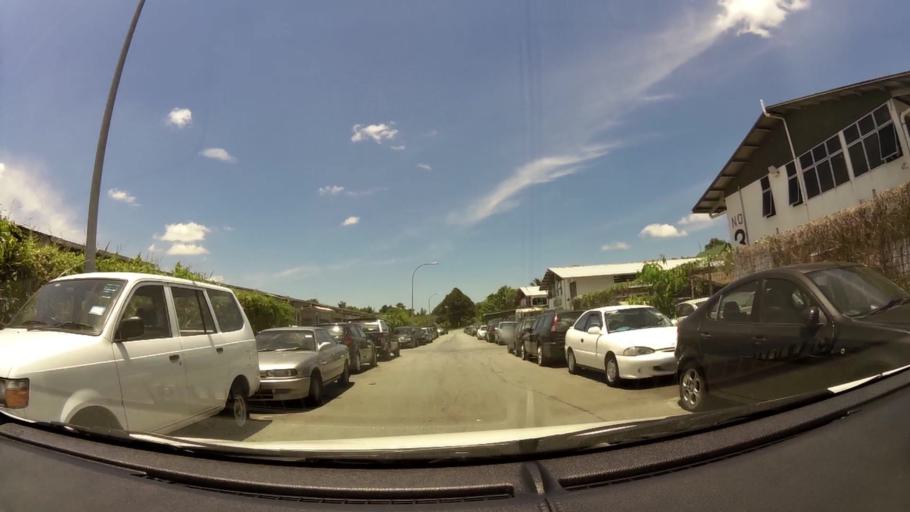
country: BN
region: Brunei and Muara
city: Bandar Seri Begawan
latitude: 4.9404
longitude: 114.9578
